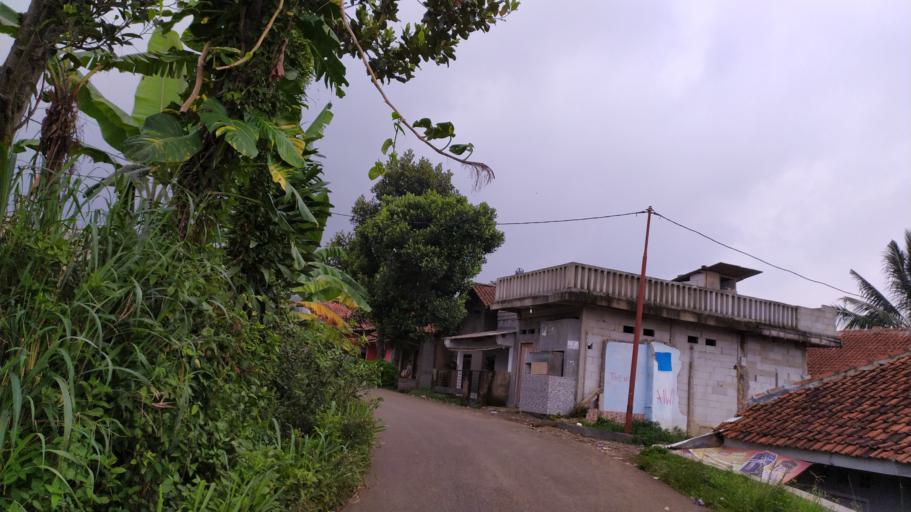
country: ID
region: West Java
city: Ciampea
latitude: -6.6376
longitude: 106.7071
